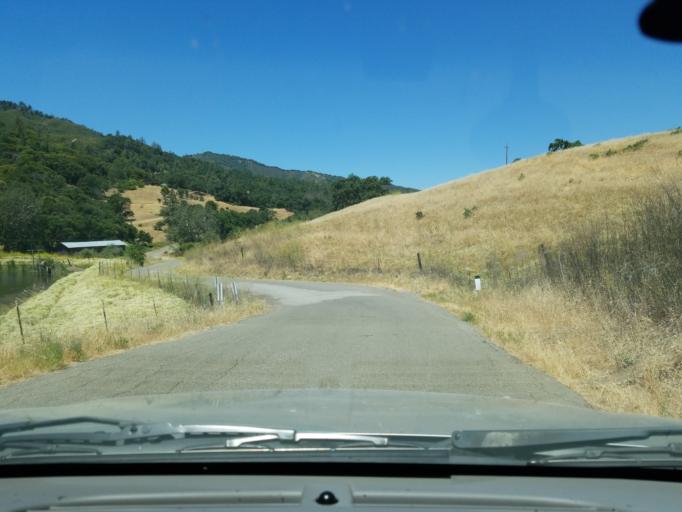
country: US
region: California
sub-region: Monterey County
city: Gonzales
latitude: 36.3375
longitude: -121.5329
